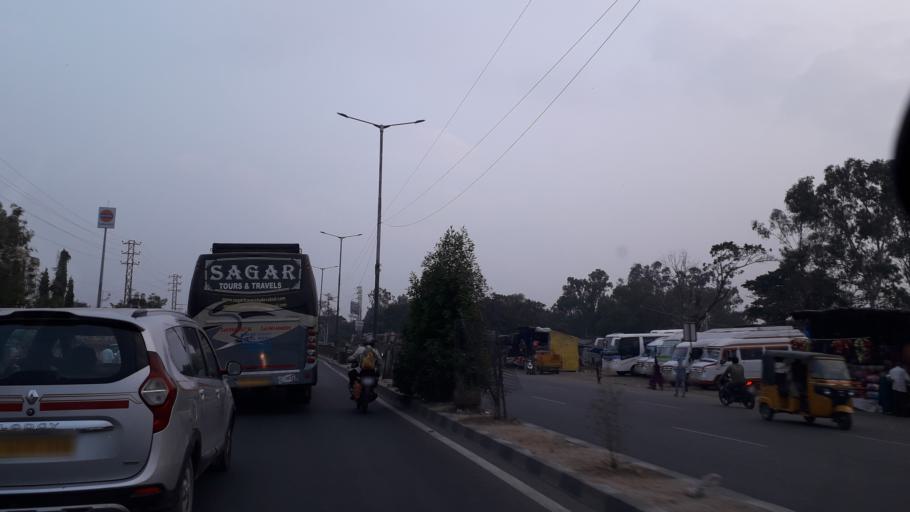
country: IN
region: Telangana
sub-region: Medak
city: Serilingampalle
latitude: 17.4979
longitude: 78.3143
